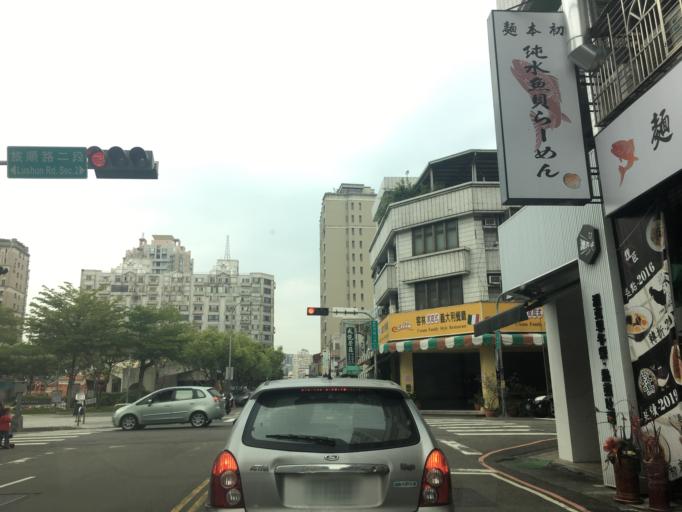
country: TW
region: Taiwan
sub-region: Taichung City
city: Taichung
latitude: 24.1740
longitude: 120.6879
